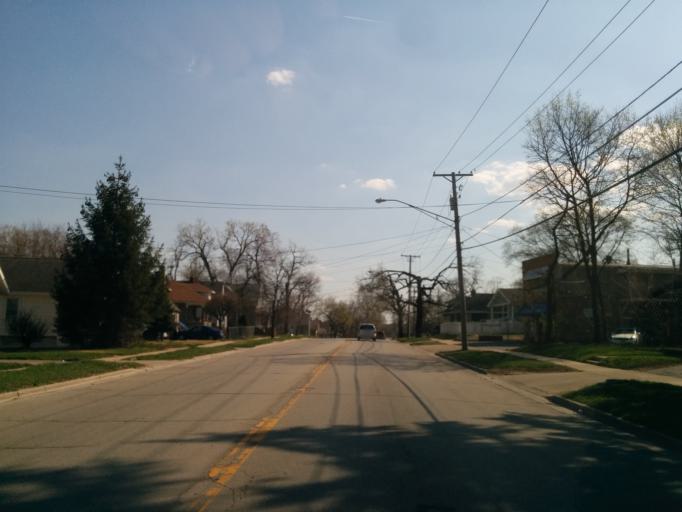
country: US
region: Illinois
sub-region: Kane County
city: Elgin
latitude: 42.0189
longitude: -88.2673
